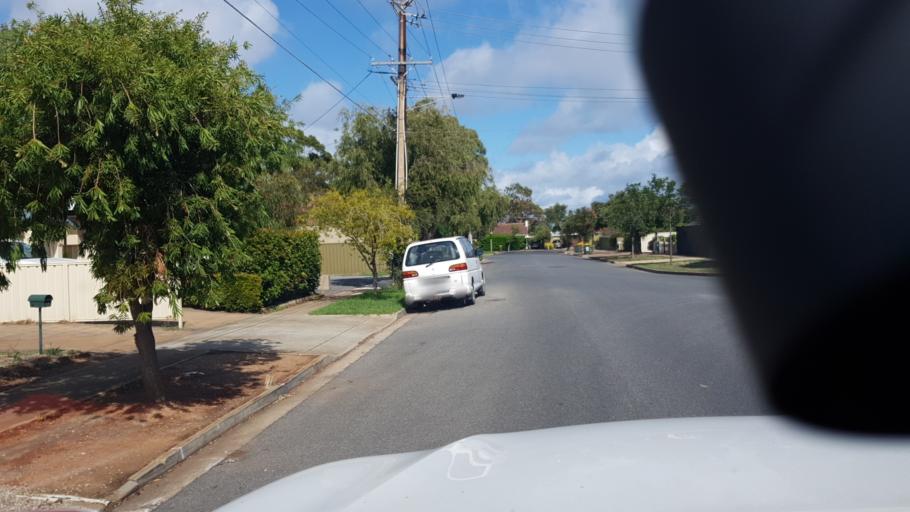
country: AU
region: South Australia
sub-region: Holdfast Bay
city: Seacliff Park
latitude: -35.0224
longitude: 138.5333
